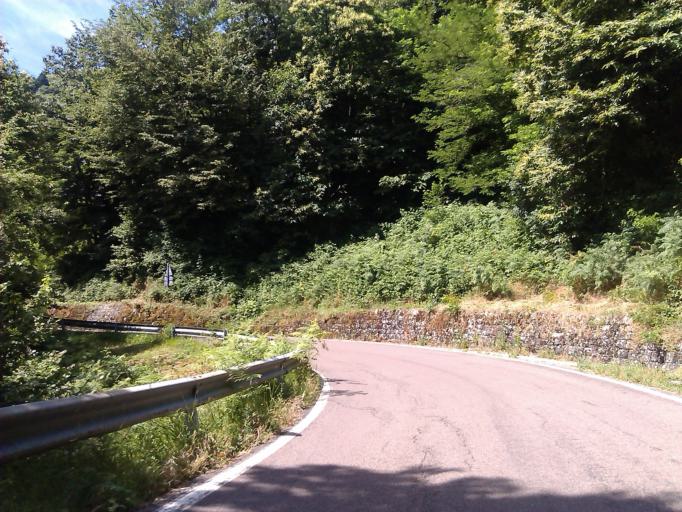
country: IT
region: Tuscany
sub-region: Provincia di Pistoia
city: Sambuca Pistoiese
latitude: 44.1121
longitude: 11.0393
